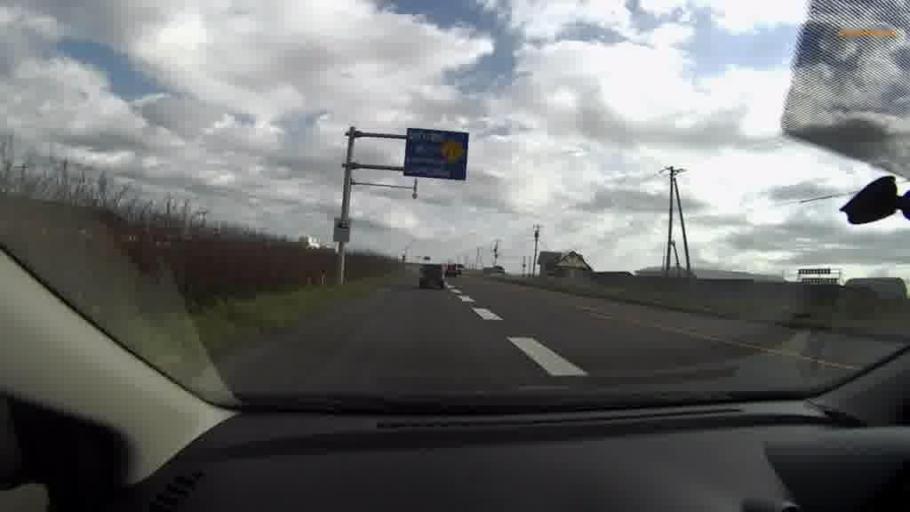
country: JP
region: Hokkaido
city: Kushiro
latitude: 42.9679
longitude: 144.1193
